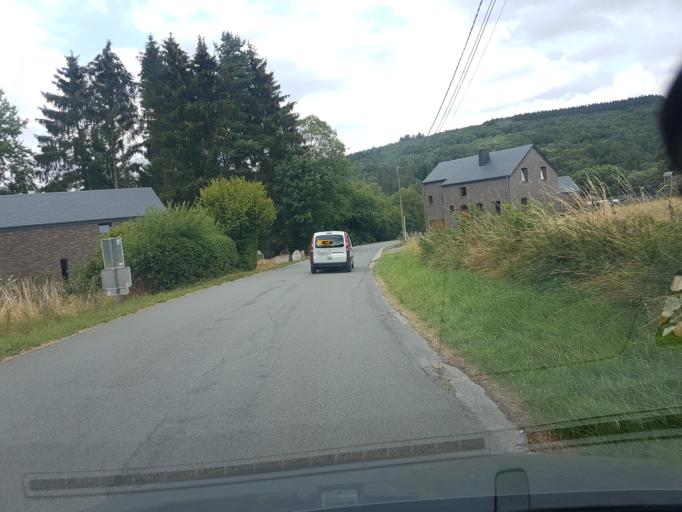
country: BE
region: Wallonia
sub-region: Province du Luxembourg
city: Manhay
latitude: 50.2613
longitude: 5.6522
